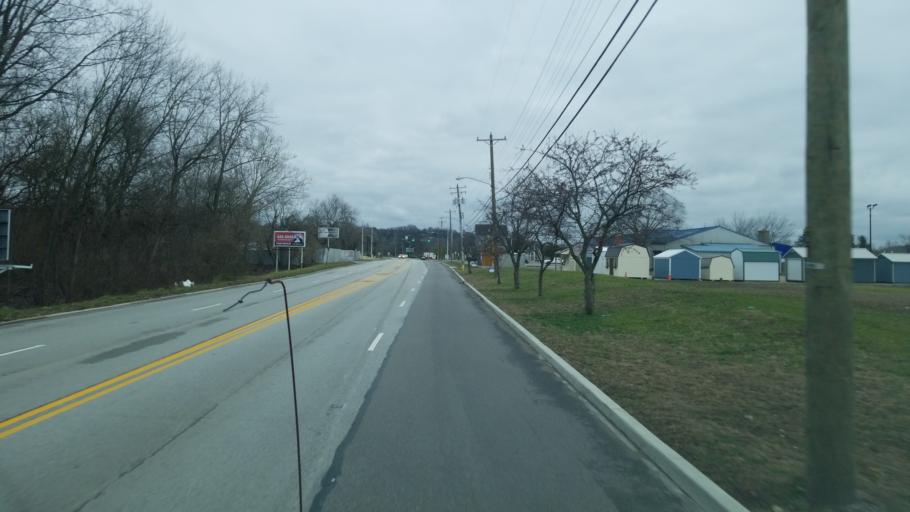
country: US
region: Kentucky
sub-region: Campbell County
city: Fort Thomas
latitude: 39.0952
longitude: -84.4291
